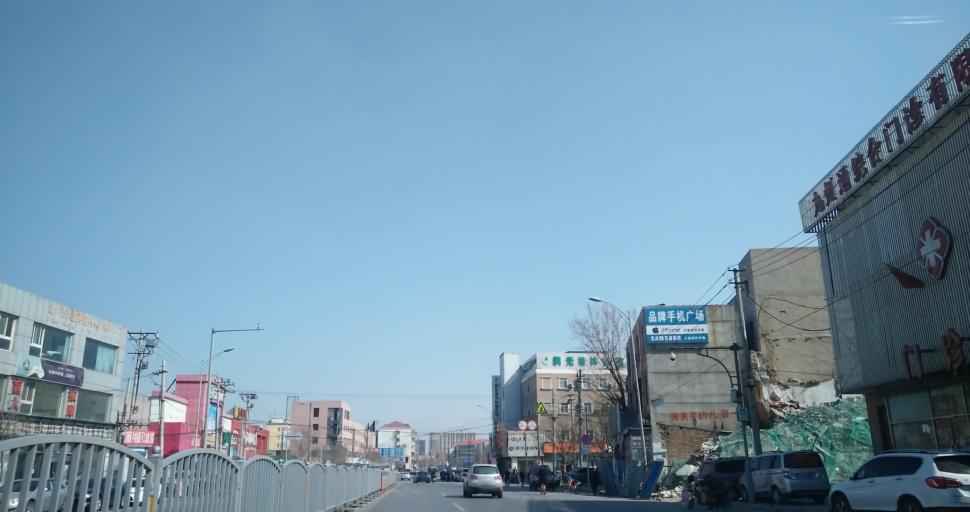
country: CN
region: Beijing
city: Jiugong
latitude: 39.8033
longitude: 116.4317
